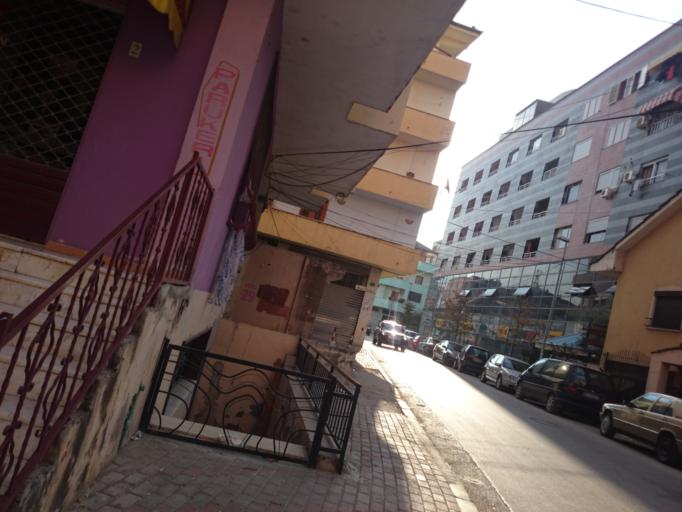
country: AL
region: Tirane
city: Tirana
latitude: 41.3192
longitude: 19.8003
